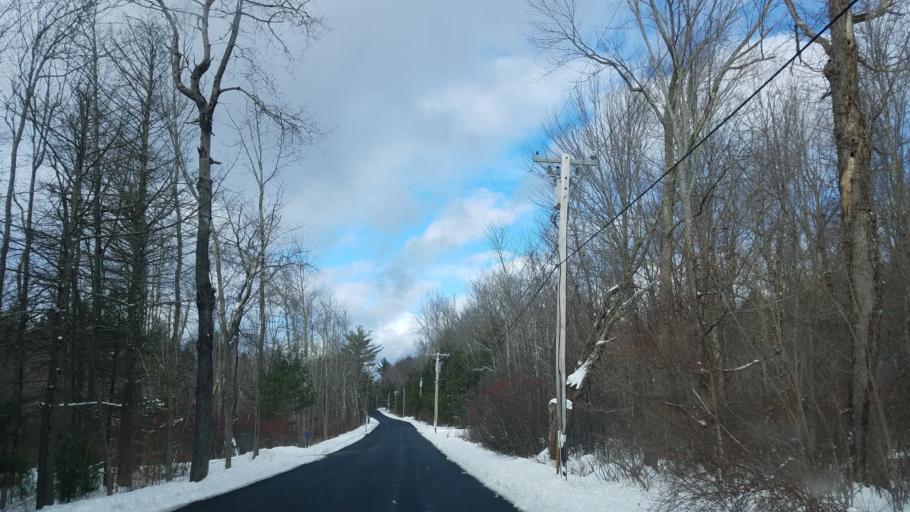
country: US
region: Connecticut
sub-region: Litchfield County
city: Winsted
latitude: 41.9822
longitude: -73.0851
